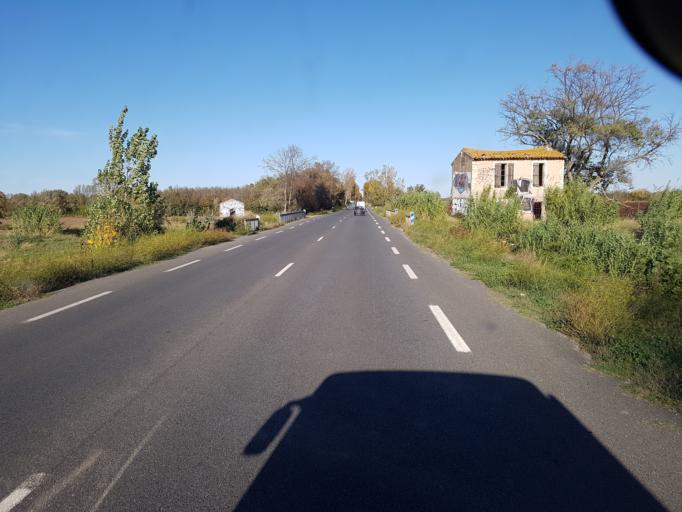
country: FR
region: Languedoc-Roussillon
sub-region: Departement de l'Aude
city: Coursan
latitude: 43.2127
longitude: 3.0312
